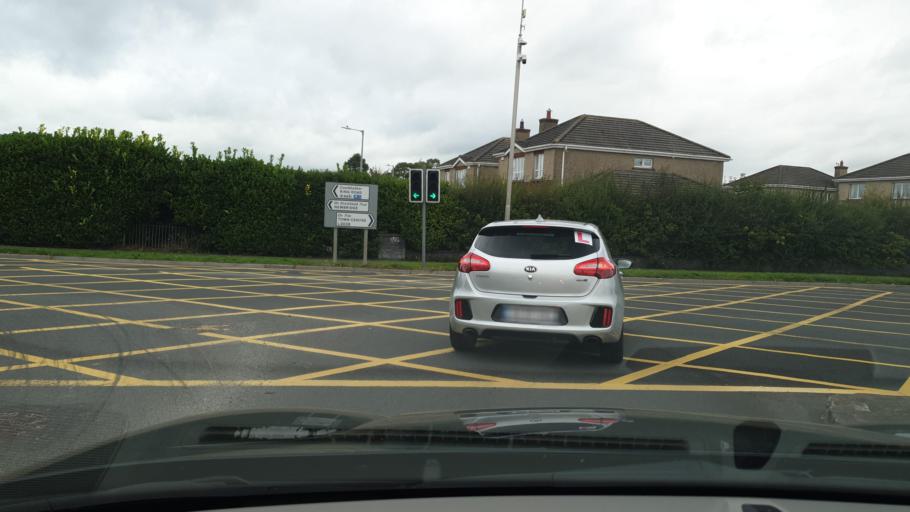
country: IE
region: Leinster
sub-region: Kildare
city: Naas
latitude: 53.2143
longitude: -6.6804
